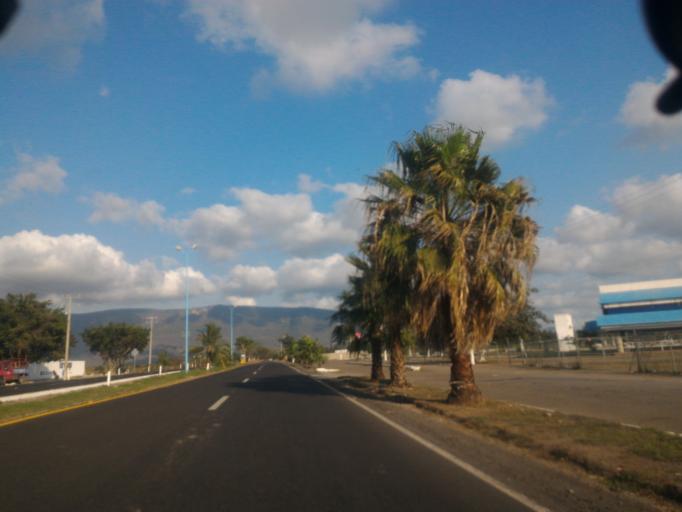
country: MX
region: Colima
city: Tecoman
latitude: 18.9437
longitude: -103.8883
